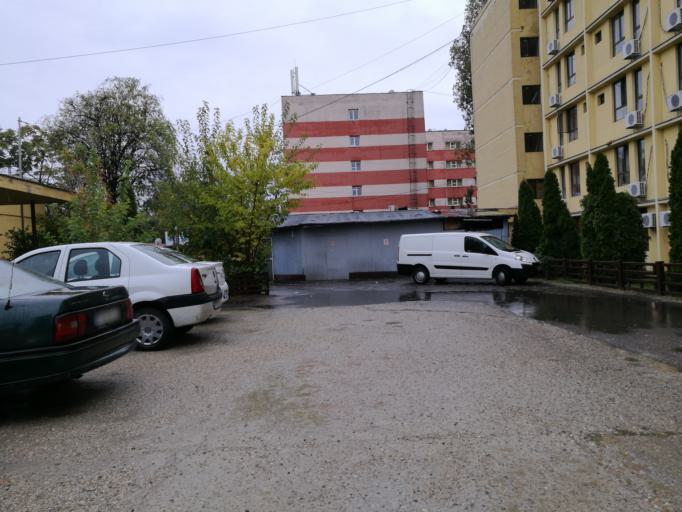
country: RO
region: Ilfov
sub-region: Comuna Chiajna
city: Rosu
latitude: 44.4458
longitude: 26.0533
